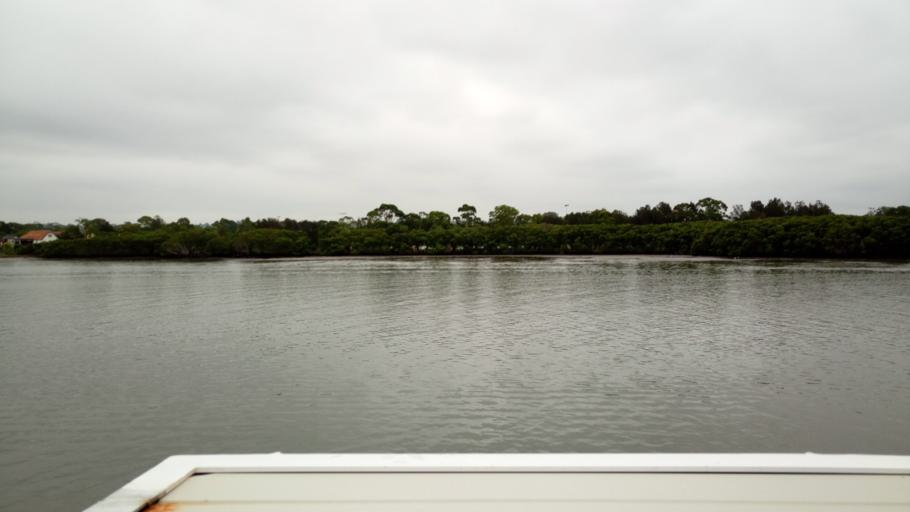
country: AU
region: New South Wales
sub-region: Canada Bay
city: Rhodes
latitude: -33.8213
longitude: 151.0830
